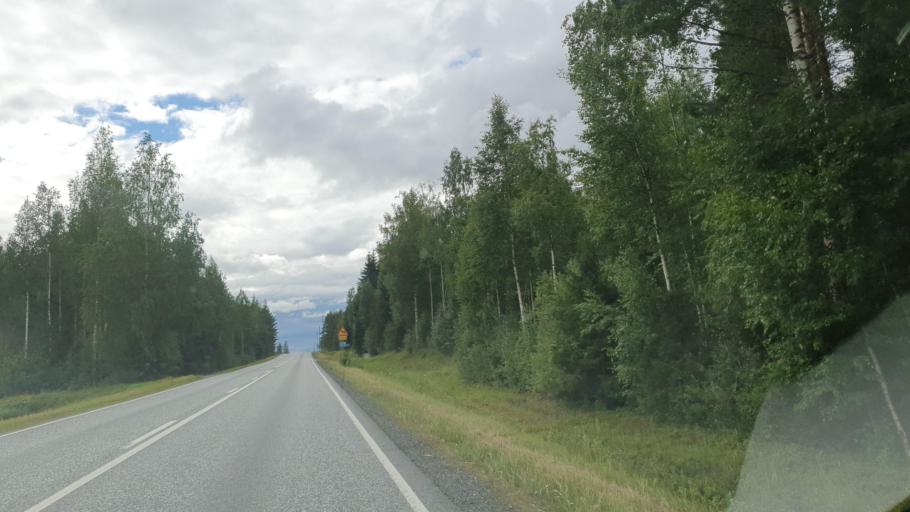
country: FI
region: Northern Savo
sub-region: Ylae-Savo
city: Iisalmi
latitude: 63.5211
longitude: 27.1789
